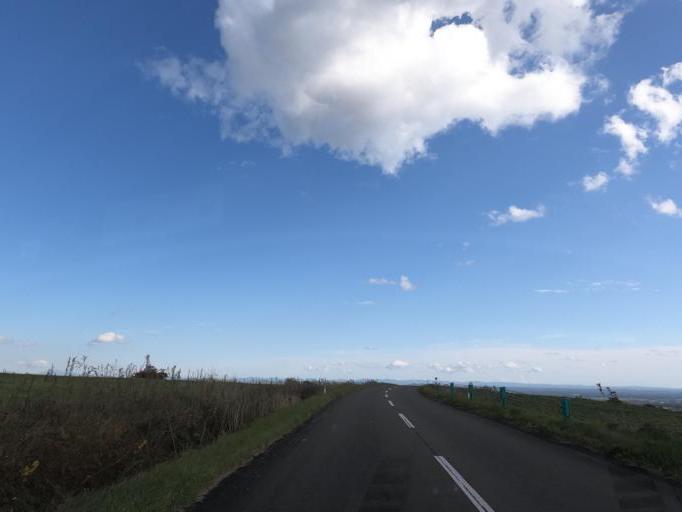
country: JP
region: Hokkaido
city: Otofuke
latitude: 43.2790
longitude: 143.2249
